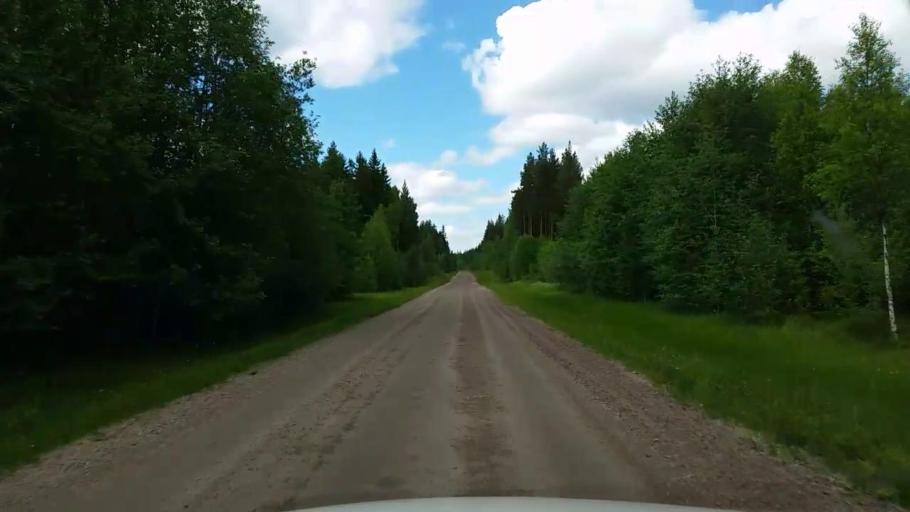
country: SE
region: Gaevleborg
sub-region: Ovanakers Kommun
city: Alfta
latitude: 61.4891
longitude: 15.9863
